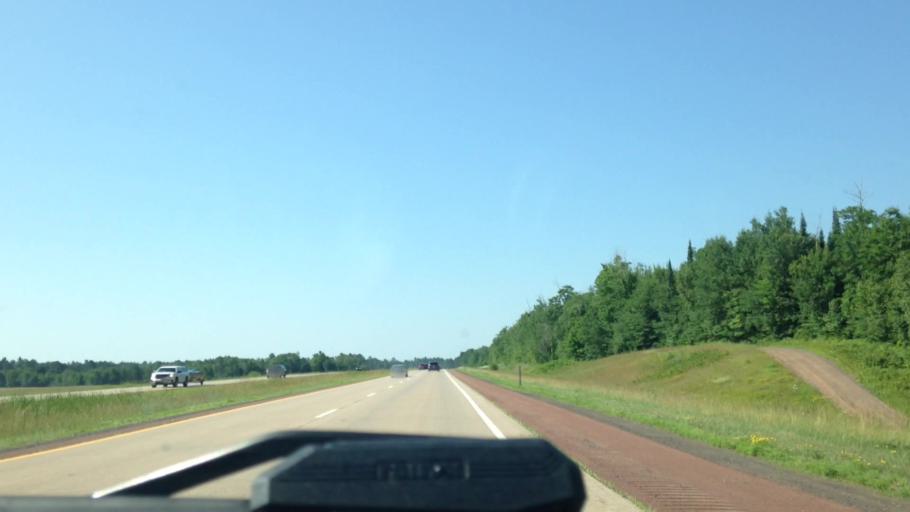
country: US
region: Wisconsin
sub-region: Douglas County
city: Lake Nebagamon
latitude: 46.3692
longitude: -91.8285
